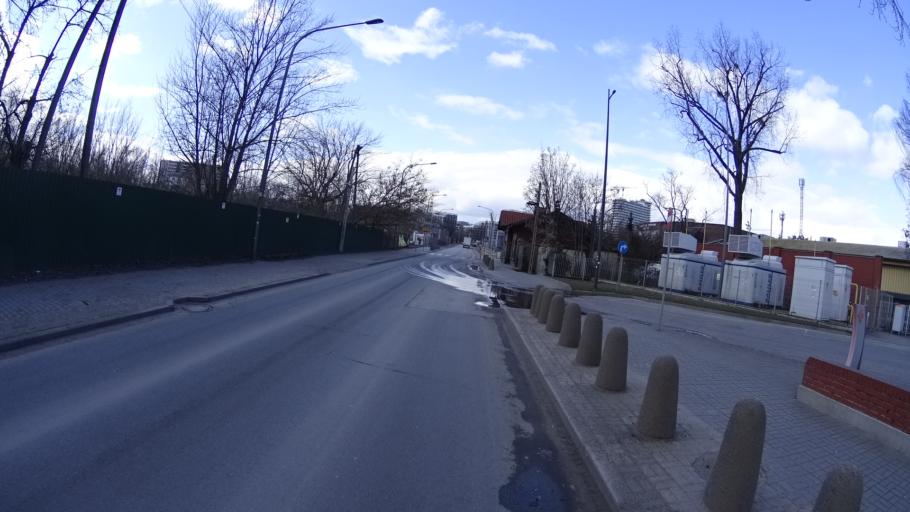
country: PL
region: Masovian Voivodeship
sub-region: Warszawa
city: Ochota
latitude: 52.2242
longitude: 20.9637
